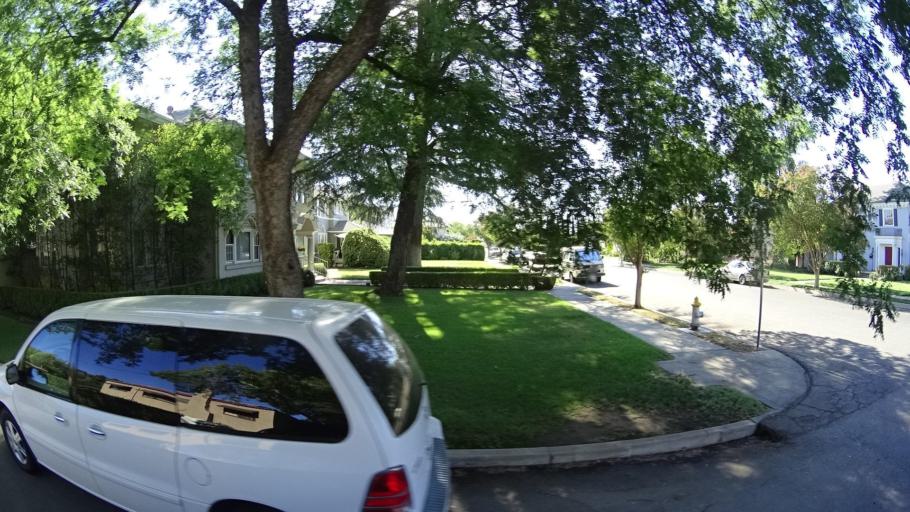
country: US
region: California
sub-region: Fresno County
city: Fresno
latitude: 36.7623
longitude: -119.8028
